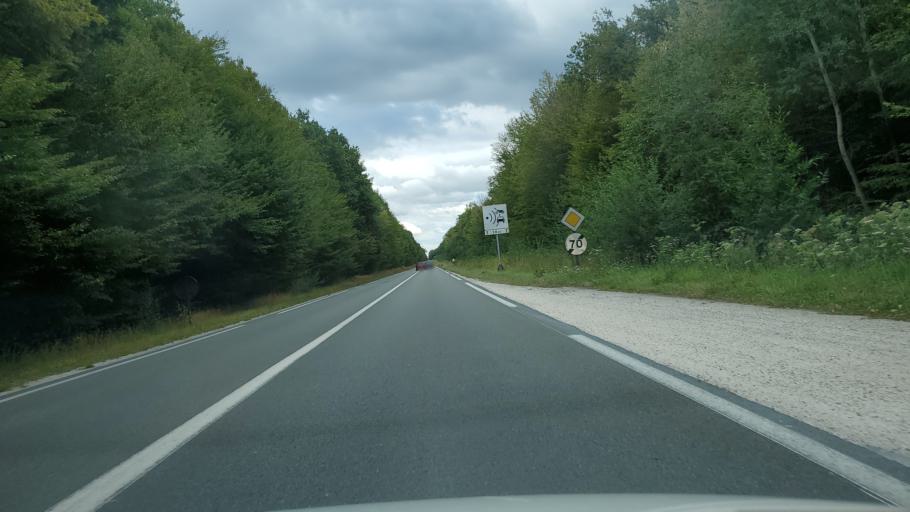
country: FR
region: Ile-de-France
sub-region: Departement de Seine-et-Marne
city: Mortcerf
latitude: 48.7747
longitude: 2.9015
